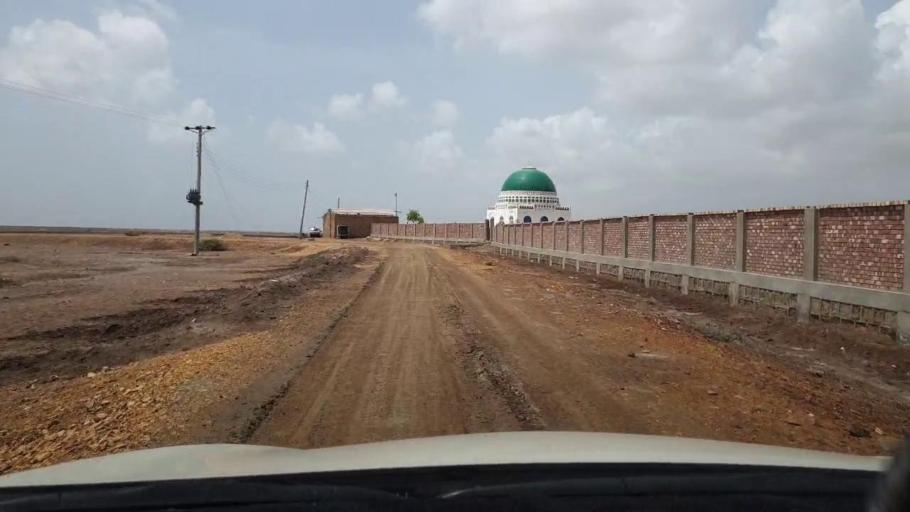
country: PK
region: Sindh
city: Kadhan
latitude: 24.3602
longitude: 68.8465
